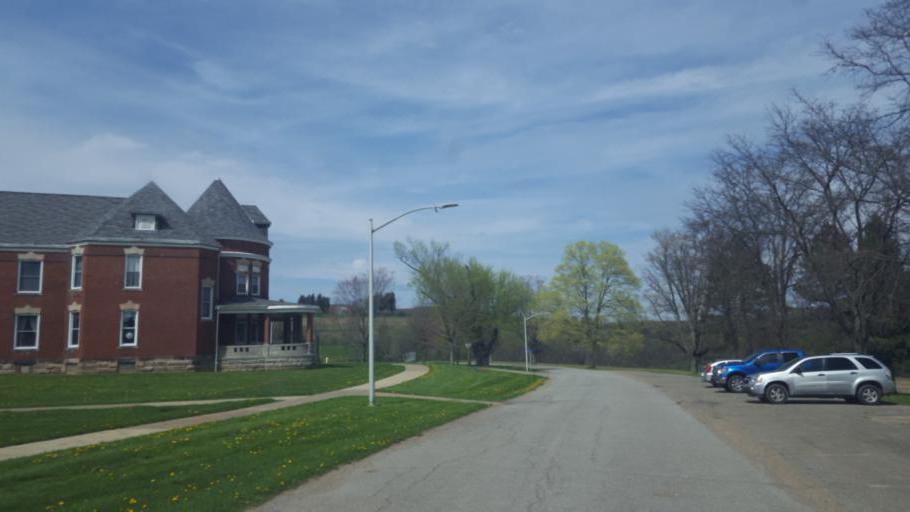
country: US
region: Pennsylvania
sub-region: Venango County
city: Sugarcreek
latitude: 41.3722
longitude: -79.9295
